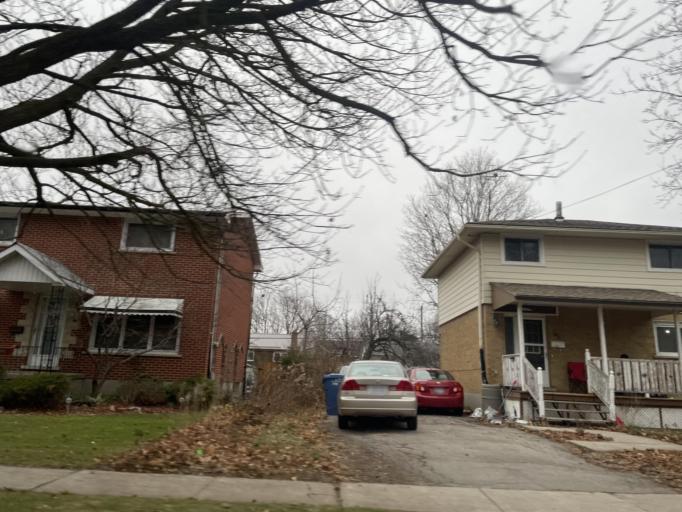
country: CA
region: Ontario
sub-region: Wellington County
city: Guelph
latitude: 43.5419
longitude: -80.2725
